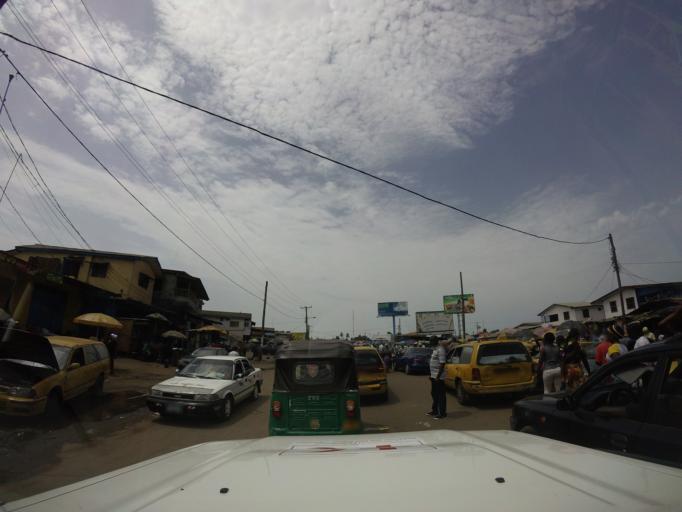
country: LR
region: Montserrado
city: Monrovia
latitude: 6.3727
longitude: -10.7877
